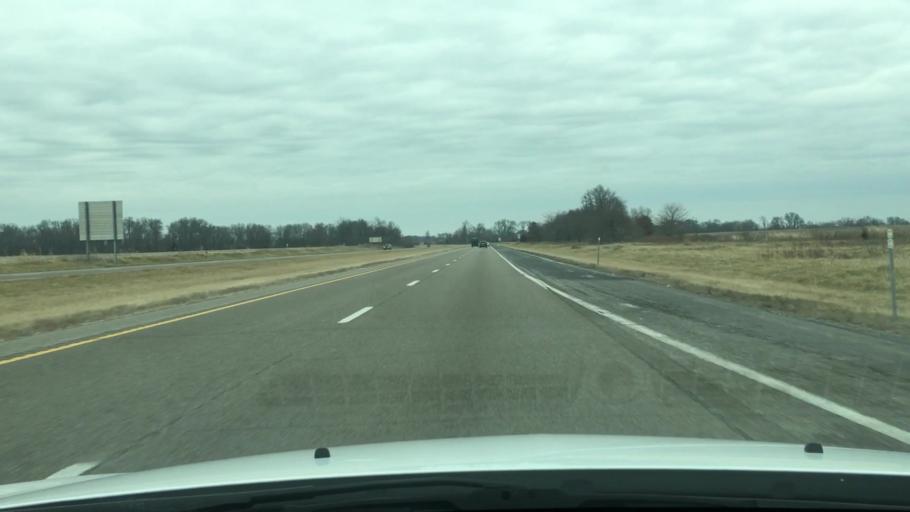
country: US
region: Missouri
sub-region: Audrain County
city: Mexico
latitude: 39.0228
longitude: -91.8857
